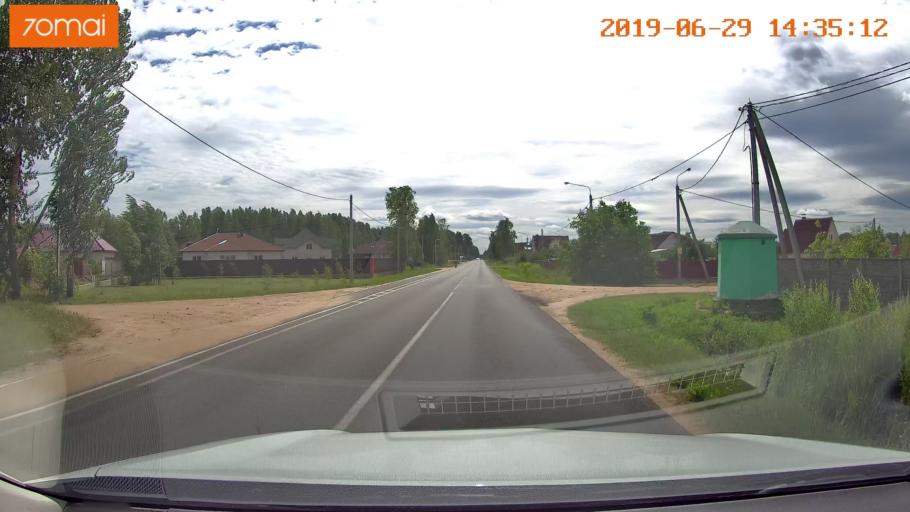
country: BY
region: Minsk
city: Starobin
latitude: 52.7618
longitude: 27.4875
